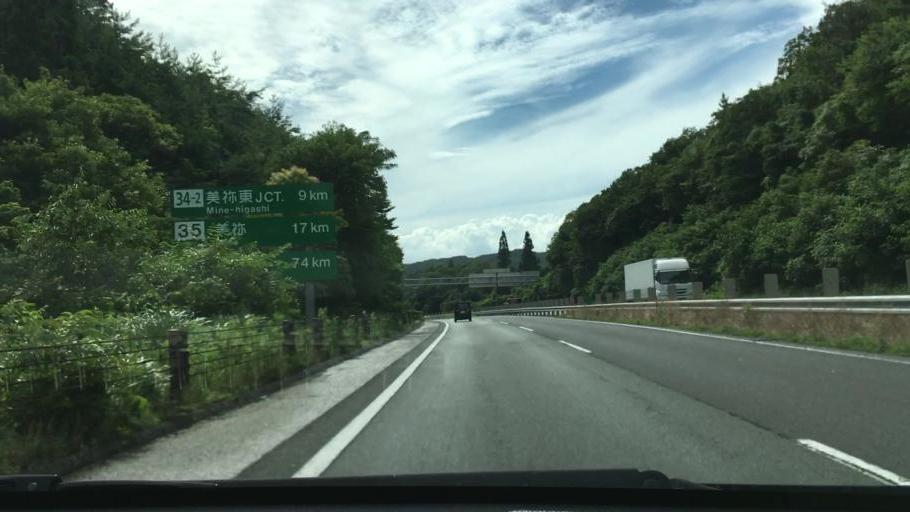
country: JP
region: Yamaguchi
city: Ogori-shimogo
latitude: 34.1262
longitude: 131.3892
